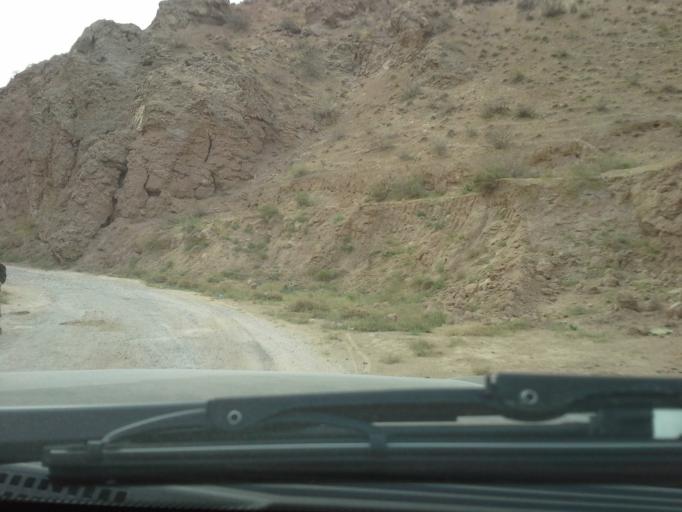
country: UZ
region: Qashqadaryo
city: Qorashina
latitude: 37.9387
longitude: 66.5356
